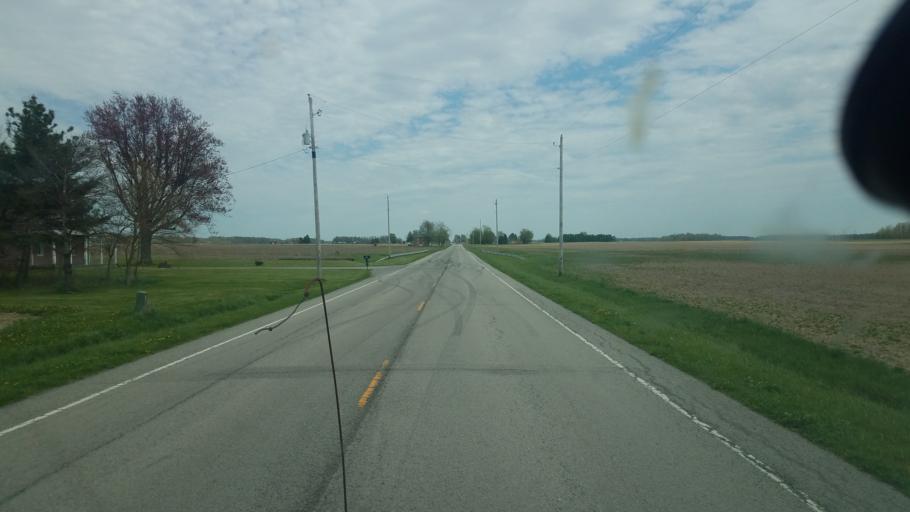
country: US
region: Ohio
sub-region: Hardin County
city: Ada
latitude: 40.8341
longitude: -83.7544
